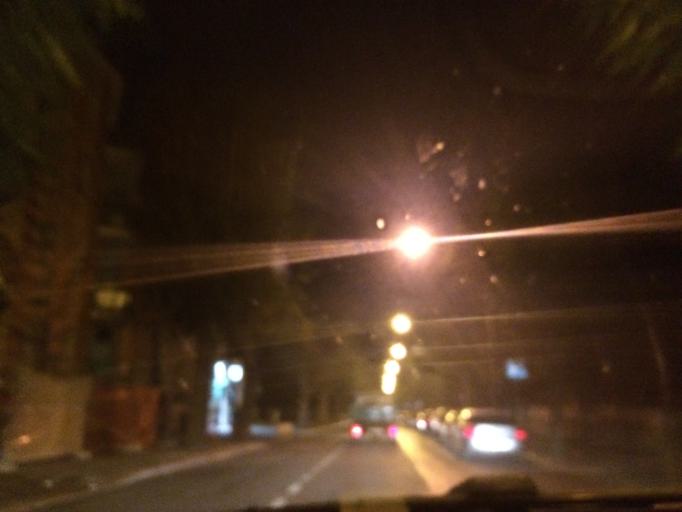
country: IT
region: Basilicate
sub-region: Provincia di Matera
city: Matera
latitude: 40.6647
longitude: 16.5947
